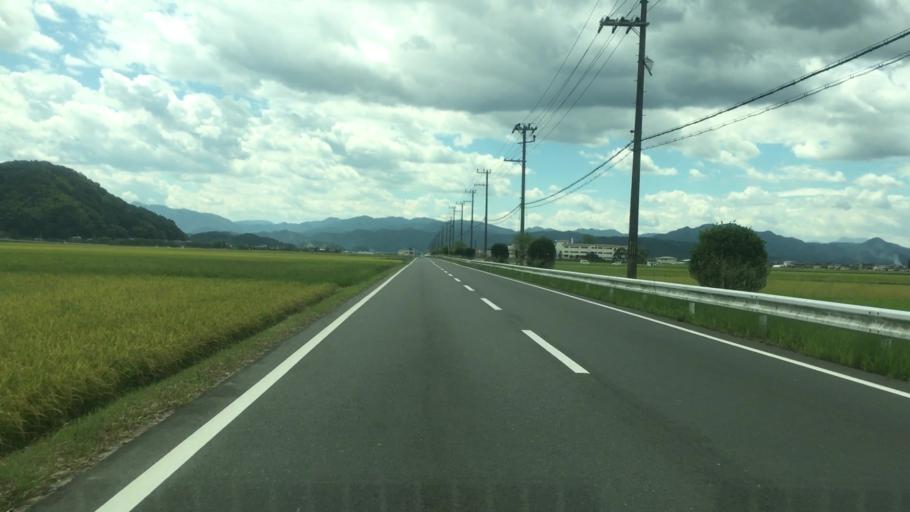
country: JP
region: Hyogo
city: Toyooka
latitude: 35.5370
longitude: 134.8397
